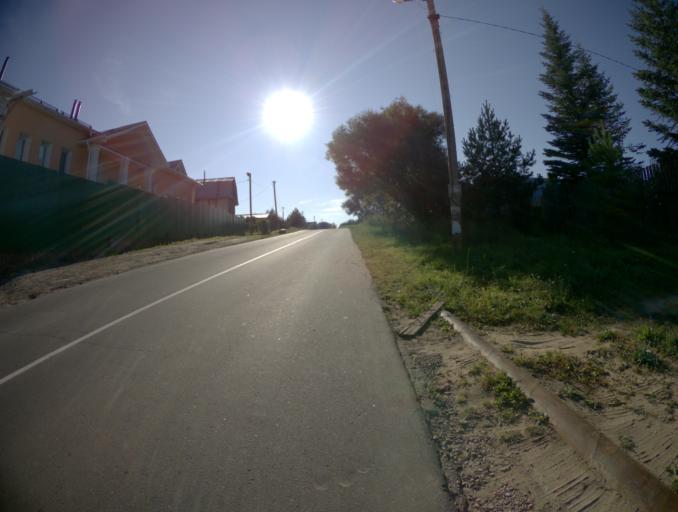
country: RU
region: Vladimir
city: Bogolyubovo
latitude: 56.2984
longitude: 40.5708
